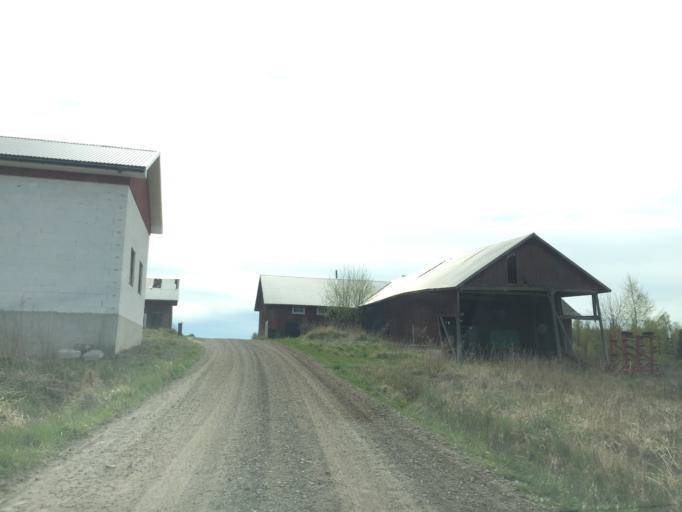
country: SE
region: OErebro
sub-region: Lekebergs Kommun
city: Fjugesta
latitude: 59.0603
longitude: 14.9155
